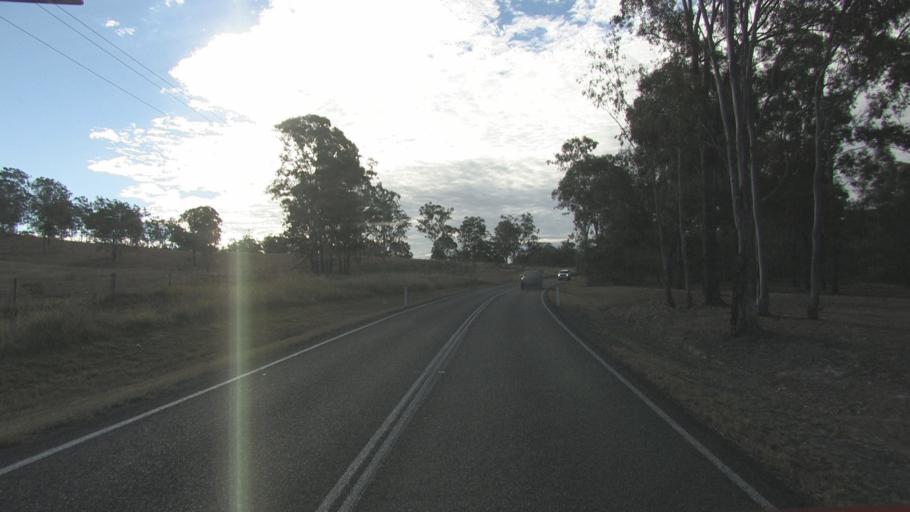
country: AU
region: Queensland
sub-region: Logan
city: Cedar Vale
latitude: -27.8751
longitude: 153.0661
